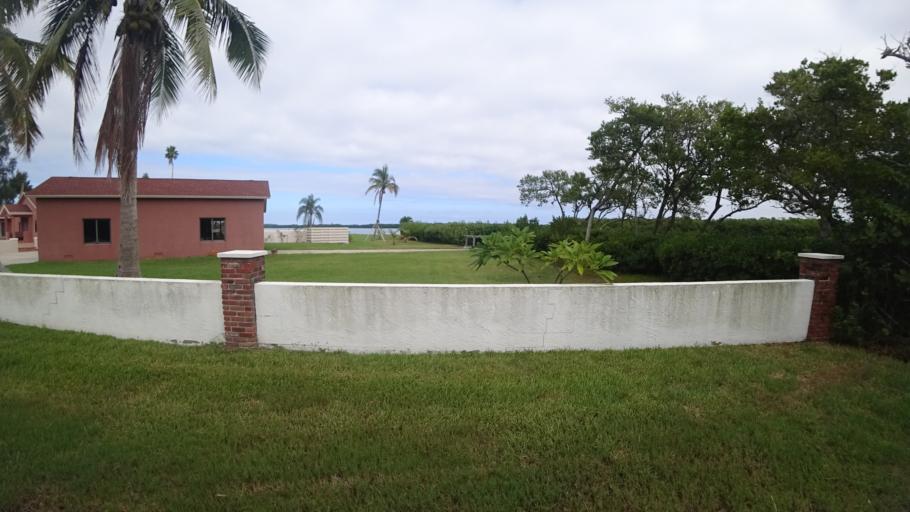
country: US
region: Florida
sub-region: Manatee County
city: Longboat Key
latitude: 27.4231
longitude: -82.6630
